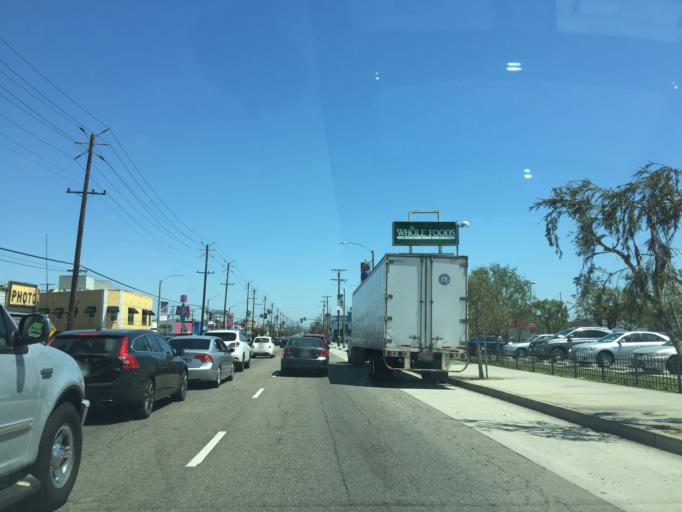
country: US
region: California
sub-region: Los Angeles County
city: Santa Monica
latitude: 34.0020
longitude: -118.4694
